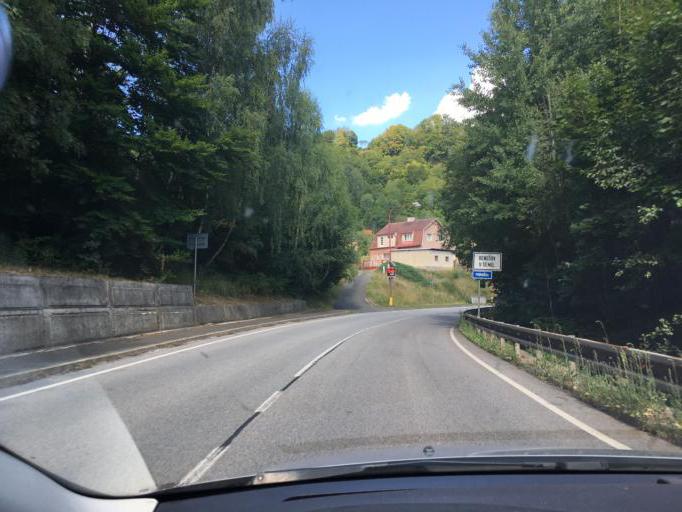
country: CZ
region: Liberecky
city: Semily
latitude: 50.6006
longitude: 15.3582
